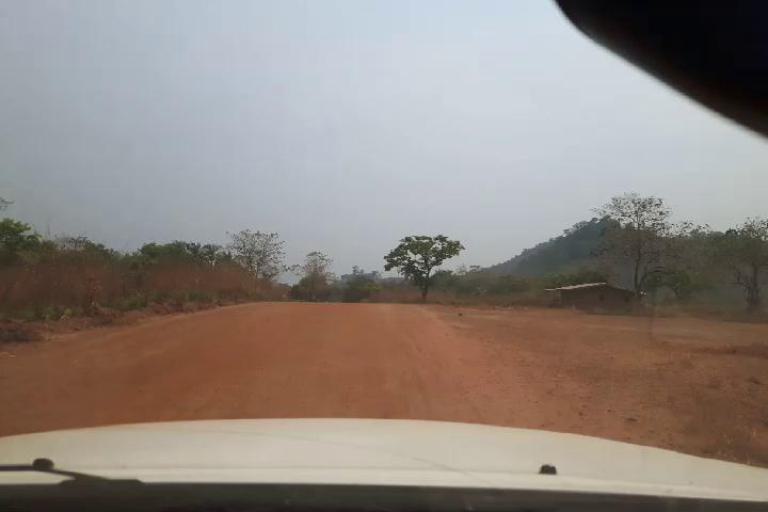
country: SL
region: Northern Province
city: Bumbuna
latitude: 9.0264
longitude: -11.7630
